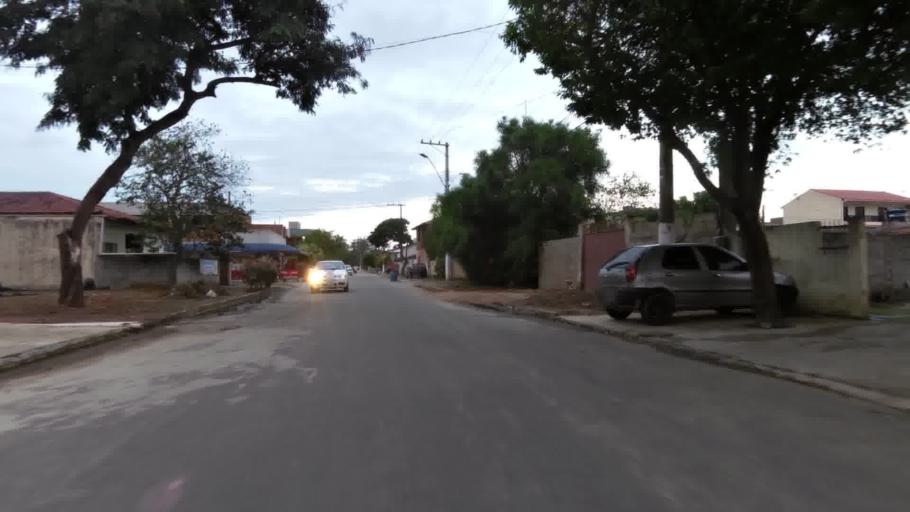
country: BR
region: Espirito Santo
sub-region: Piuma
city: Piuma
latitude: -20.8104
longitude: -40.6321
